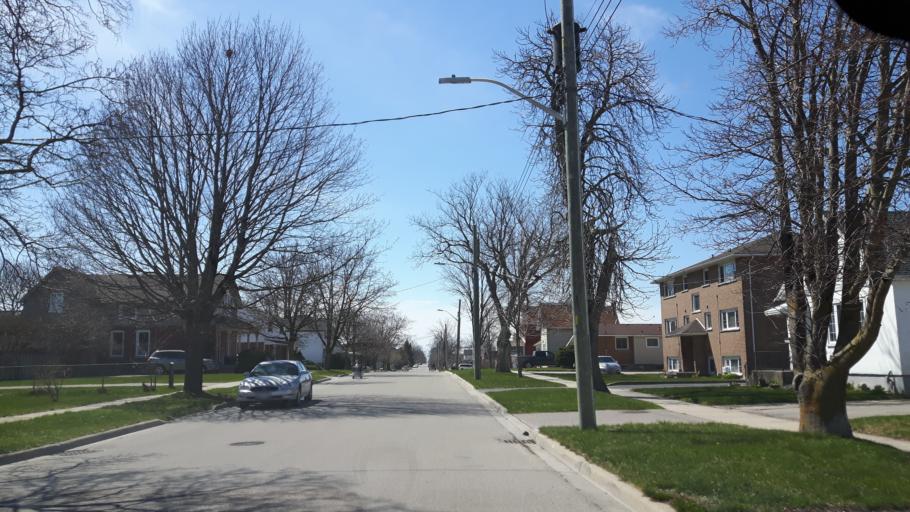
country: CA
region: Ontario
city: Goderich
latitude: 43.7395
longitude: -81.7051
